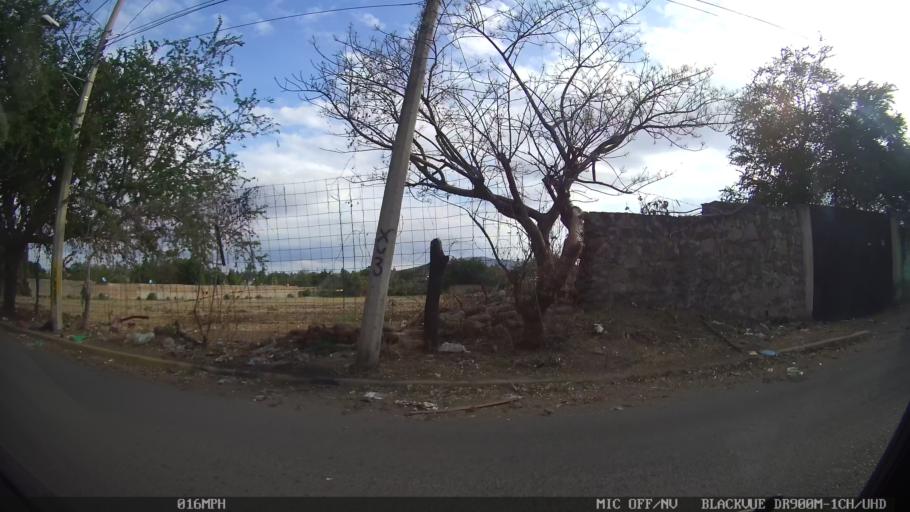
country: MX
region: Jalisco
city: Tonala
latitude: 20.6791
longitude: -103.2465
